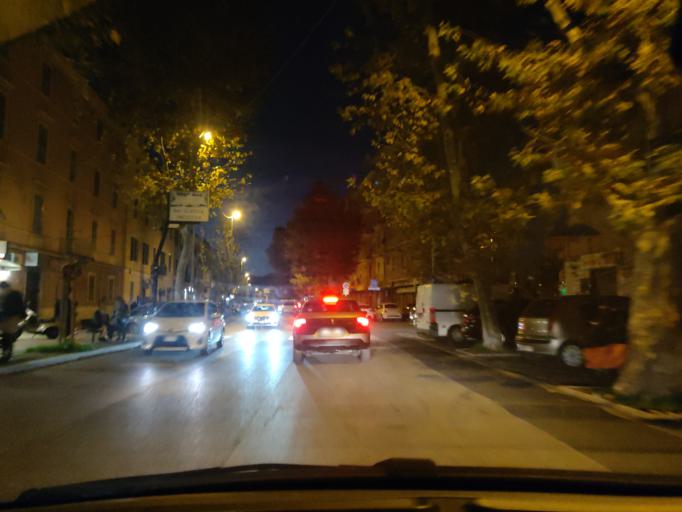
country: IT
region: Latium
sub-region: Citta metropolitana di Roma Capitale
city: Civitavecchia
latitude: 42.0923
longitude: 11.7998
